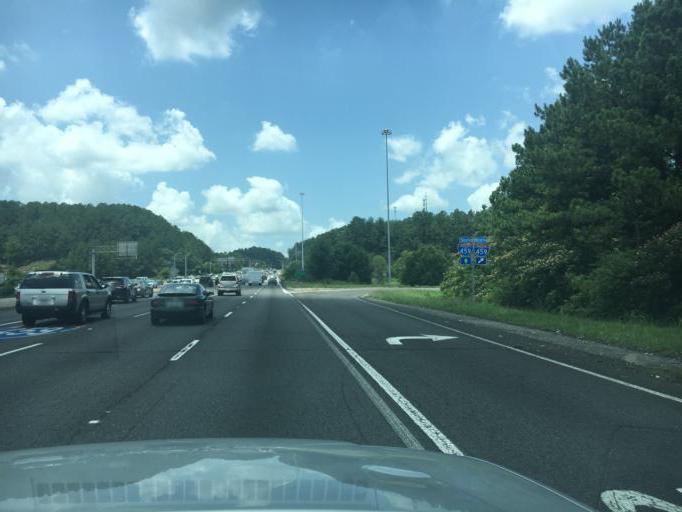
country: US
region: Alabama
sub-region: Jefferson County
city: Cahaba Heights
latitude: 33.4414
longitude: -86.7286
